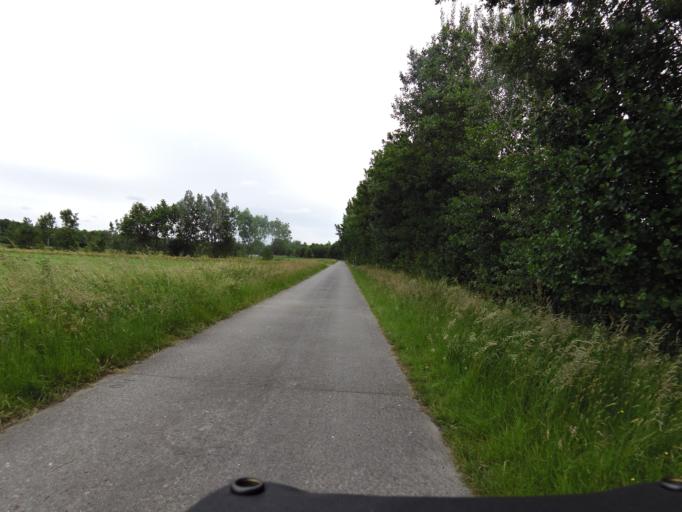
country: NL
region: North Brabant
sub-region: Gemeente Goirle
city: Goirle
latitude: 51.4508
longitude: 5.0624
